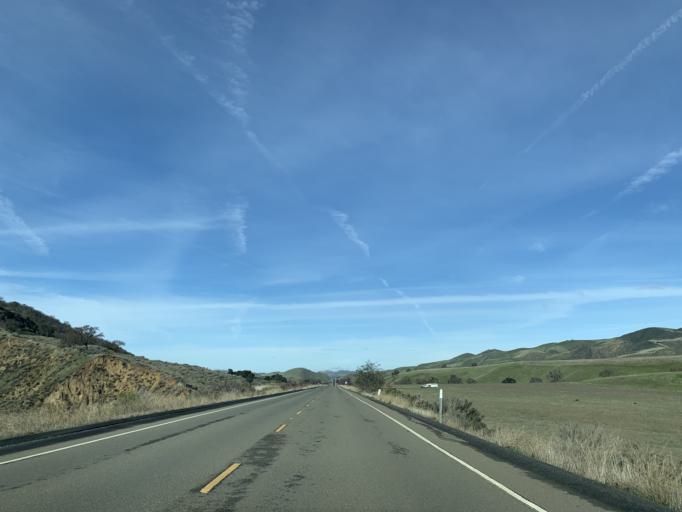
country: US
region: California
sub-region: Monterey County
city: Soledad
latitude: 36.6242
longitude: -121.2209
